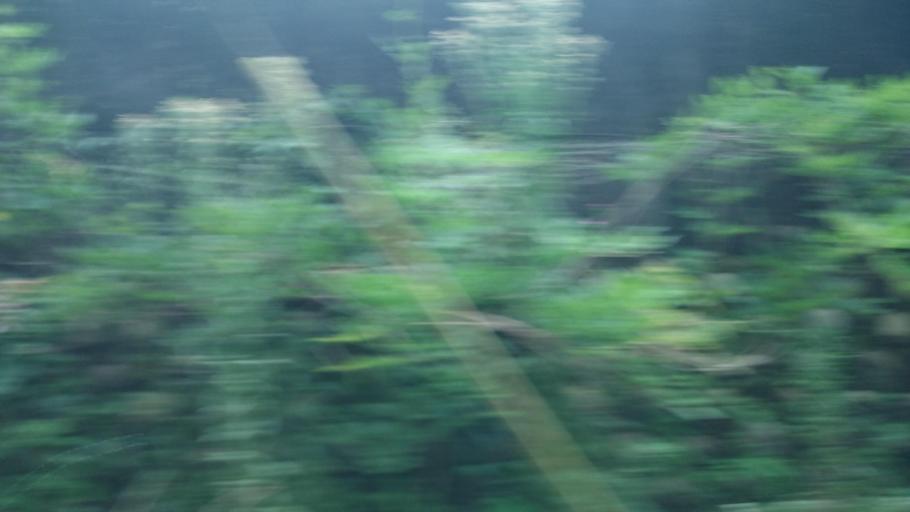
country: TW
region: Taiwan
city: Daxi
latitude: 24.9117
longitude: 121.3900
